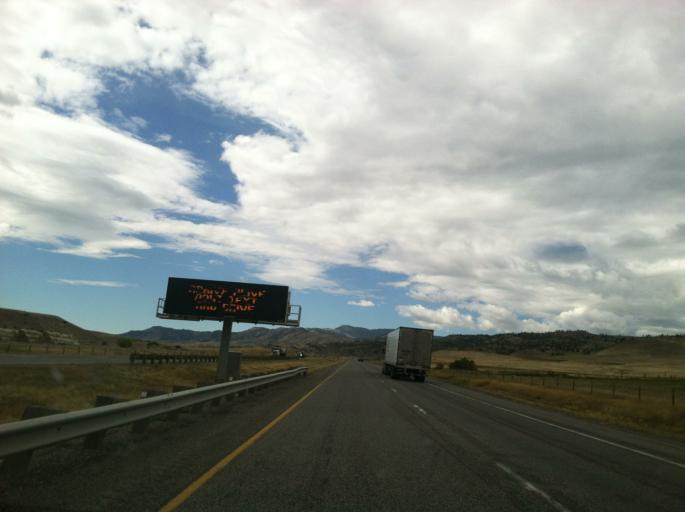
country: US
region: Montana
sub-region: Park County
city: Livingston
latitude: 45.6547
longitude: -110.6222
